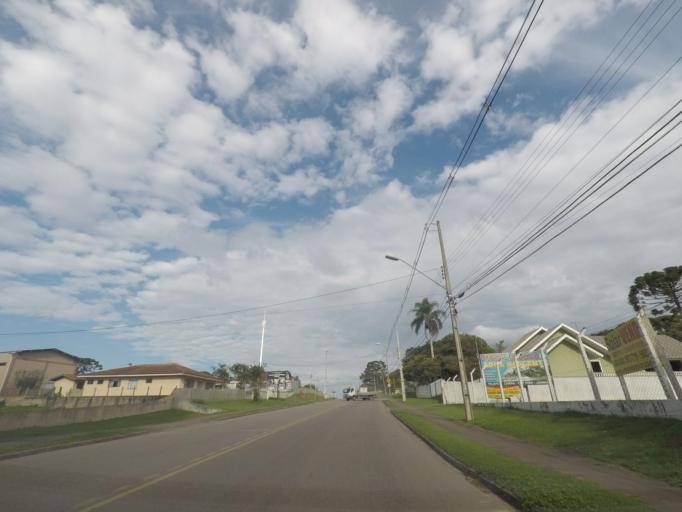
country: BR
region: Parana
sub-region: Sao Jose Dos Pinhais
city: Sao Jose dos Pinhais
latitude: -25.5716
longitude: -49.2801
